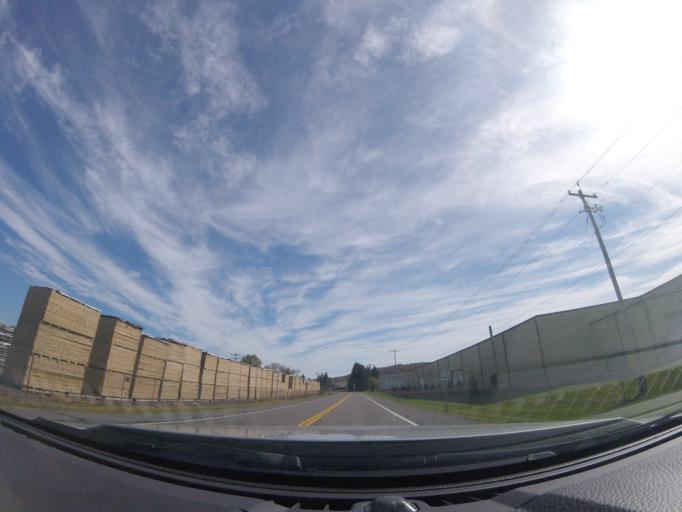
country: US
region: New York
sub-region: Cortland County
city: Munsons Corners
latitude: 42.5823
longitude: -76.2211
